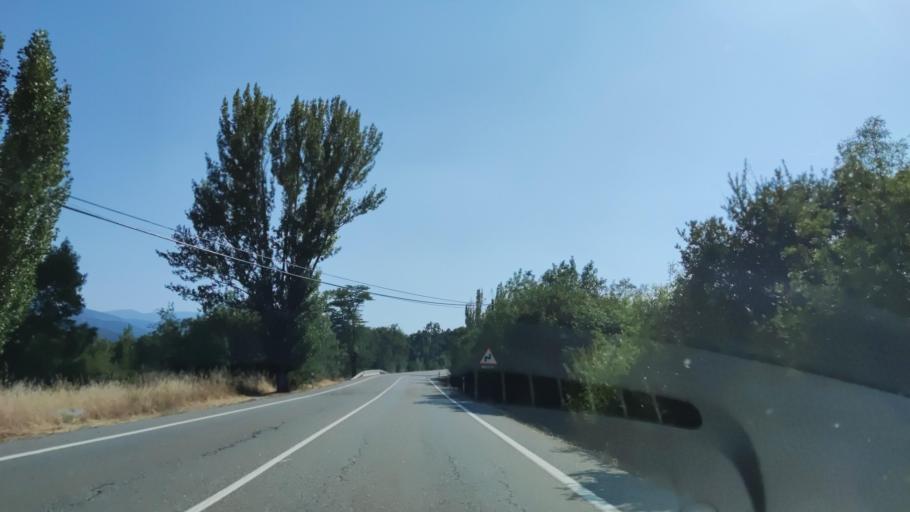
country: ES
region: Madrid
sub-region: Provincia de Madrid
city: Lozoya
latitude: 40.9473
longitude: -3.7938
